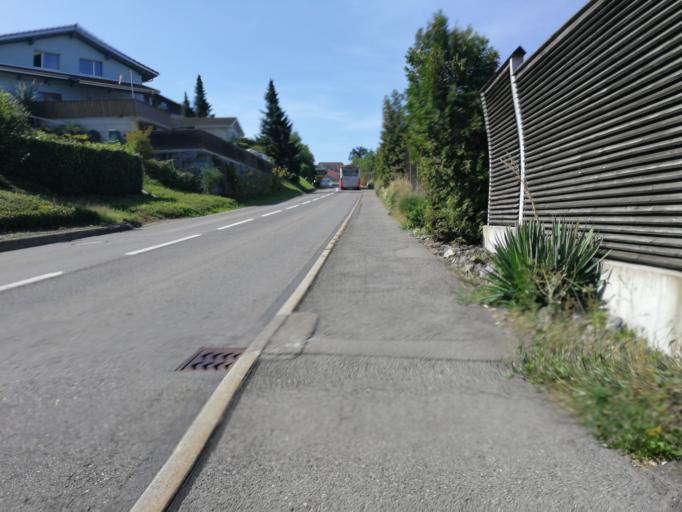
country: CH
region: Lucerne
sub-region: Lucerne-Land District
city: Weggis
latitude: 47.0535
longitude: 8.4301
